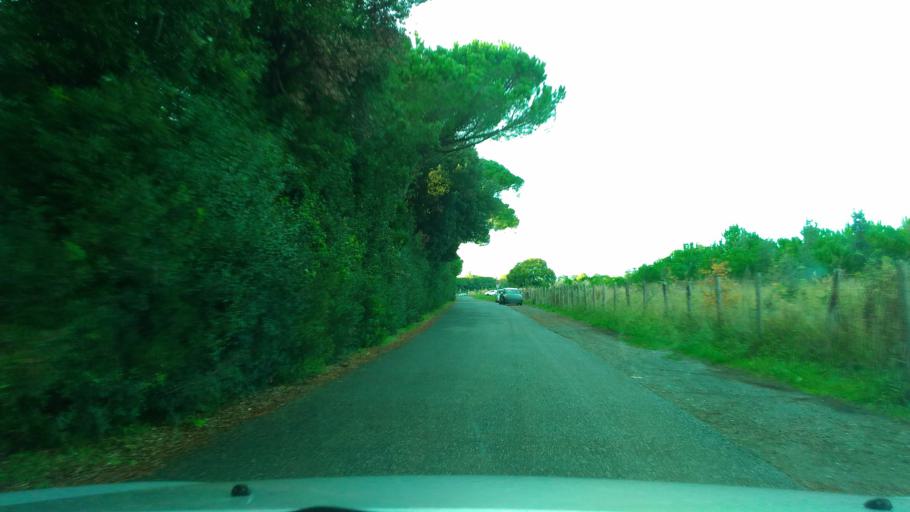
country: IT
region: Tuscany
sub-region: Provincia di Livorno
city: Cecina
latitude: 43.2871
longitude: 10.5099
